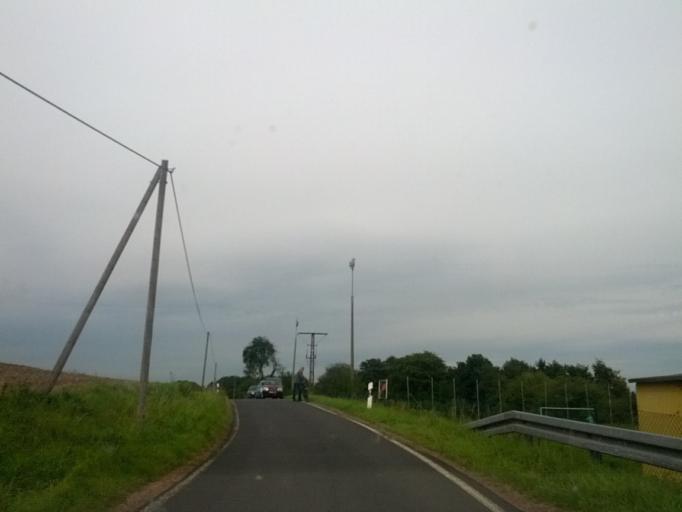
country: DE
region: Thuringia
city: Wolfsburg-Unkeroda
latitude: 50.9071
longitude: 10.2623
